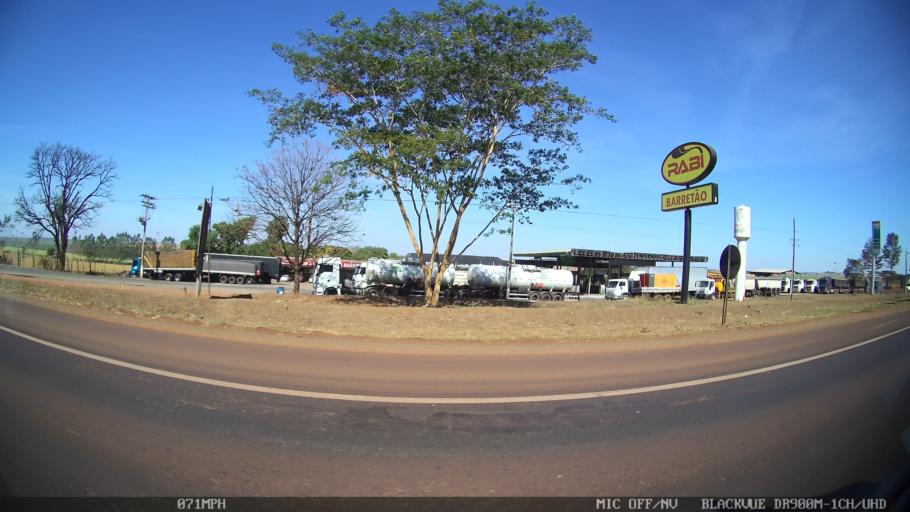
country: BR
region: Sao Paulo
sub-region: Barretos
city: Barretos
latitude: -20.5002
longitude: -48.5401
